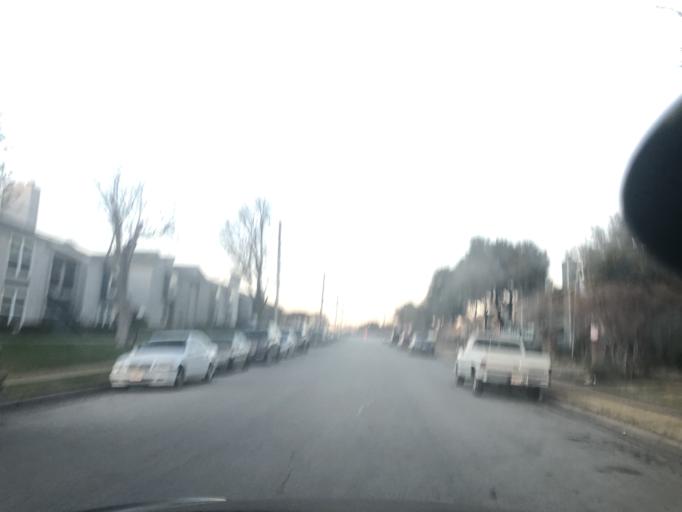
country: US
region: Texas
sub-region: Tarrant County
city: White Settlement
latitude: 32.7259
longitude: -97.4692
